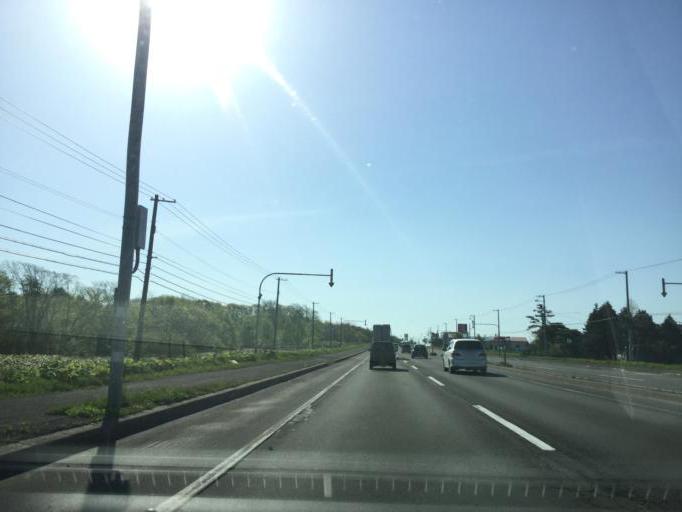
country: JP
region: Hokkaido
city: Kitahiroshima
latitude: 43.0098
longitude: 141.5152
